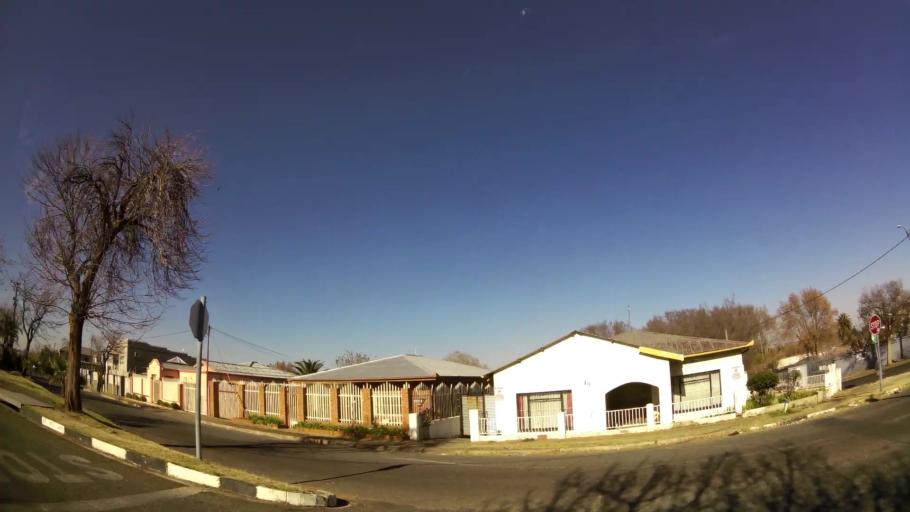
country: ZA
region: Gauteng
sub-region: City of Johannesburg Metropolitan Municipality
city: Johannesburg
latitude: -26.1992
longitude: 27.9938
